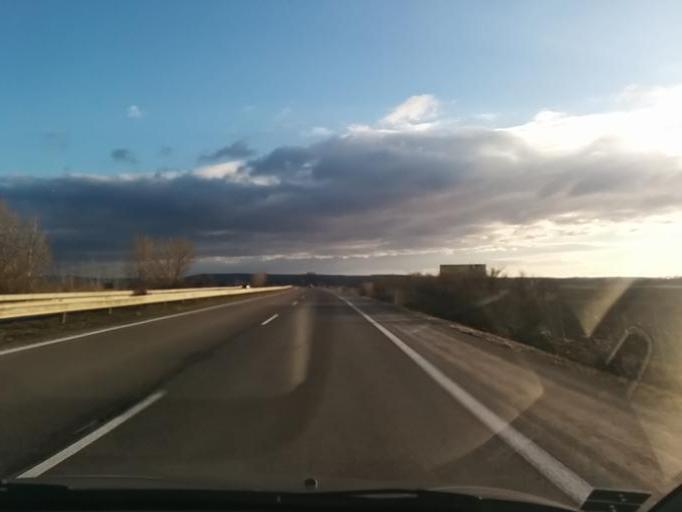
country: SK
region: Trnavsky
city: Leopoldov
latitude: 48.3683
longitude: 17.7129
